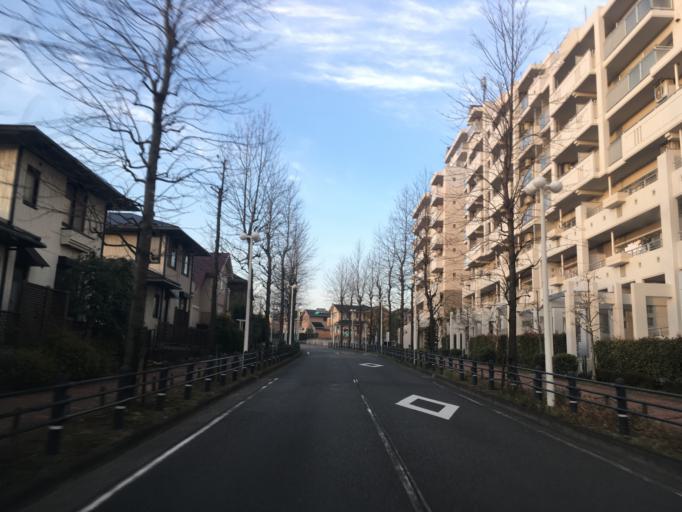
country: JP
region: Tokyo
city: Hino
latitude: 35.6160
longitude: 139.3907
